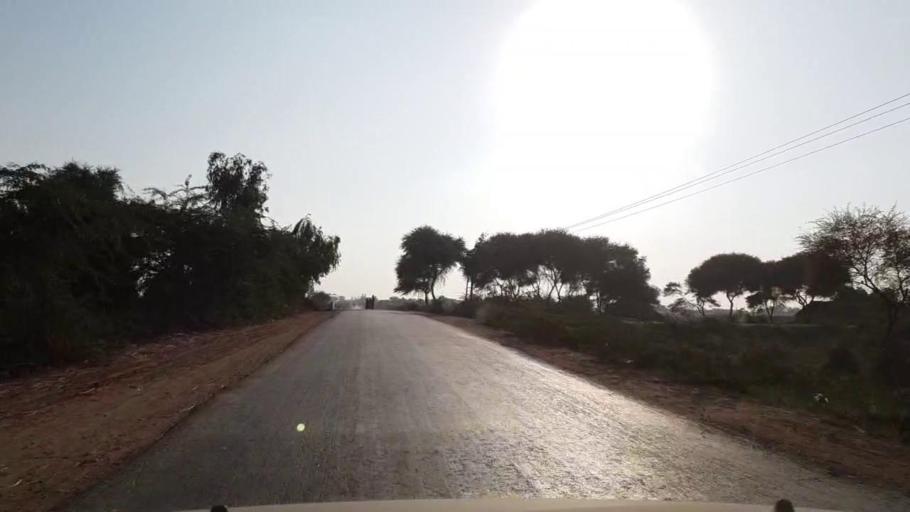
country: PK
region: Sindh
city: Mirpur Batoro
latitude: 24.7421
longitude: 68.2602
